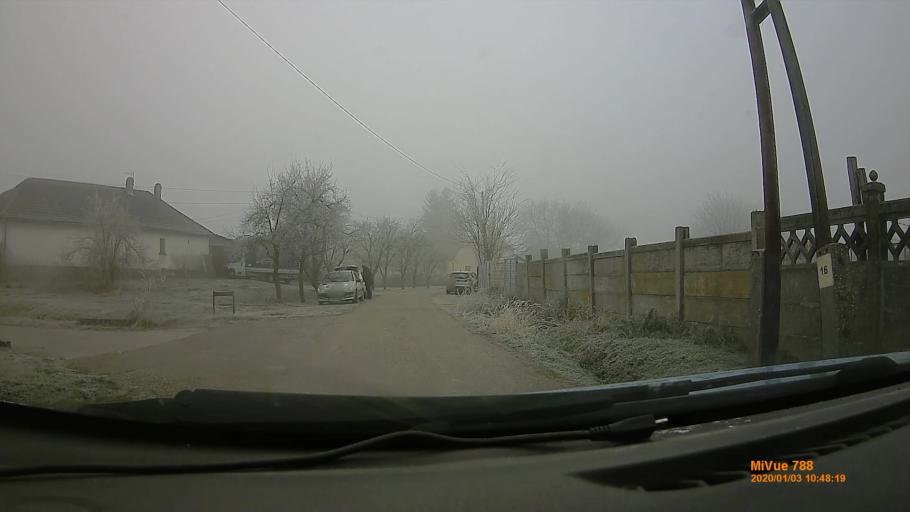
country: HU
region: Tolna
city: Bataszek
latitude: 46.2040
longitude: 18.7327
